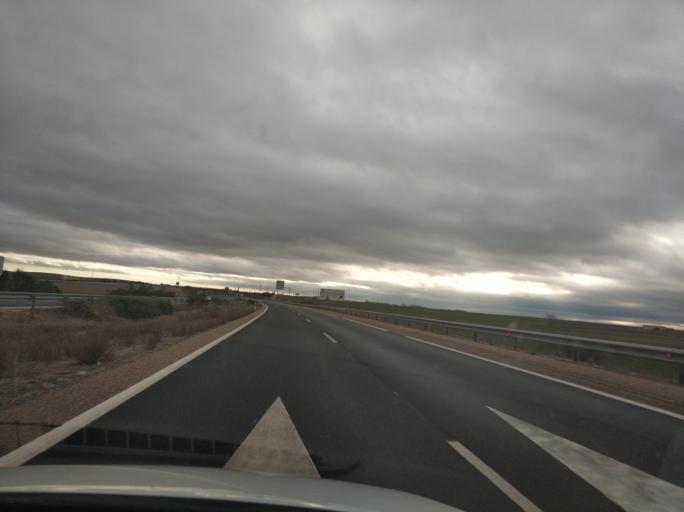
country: ES
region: Castille and Leon
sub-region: Provincia de Salamanca
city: Pajares de la Laguna
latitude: 41.0985
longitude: -5.5001
